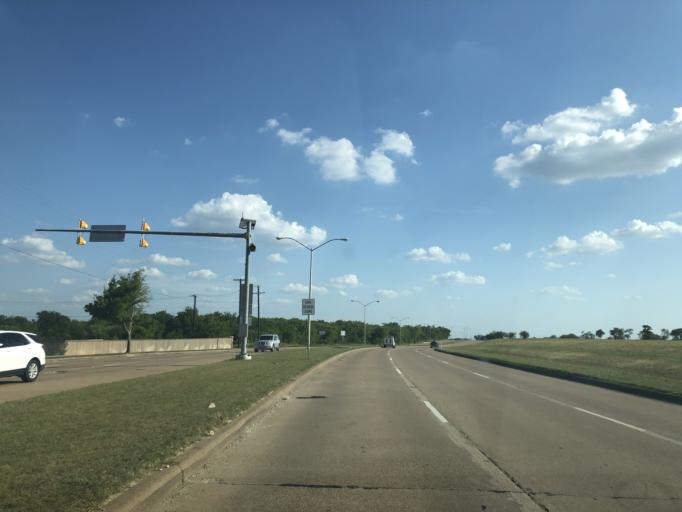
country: US
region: Texas
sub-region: Tarrant County
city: Saginaw
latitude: 32.8356
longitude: -97.3844
